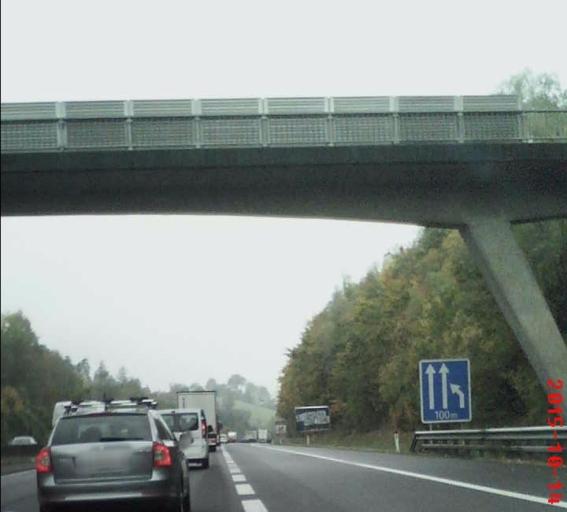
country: AT
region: Upper Austria
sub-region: Wels-Land
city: Gunskirchen
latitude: 48.1848
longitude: 13.9696
